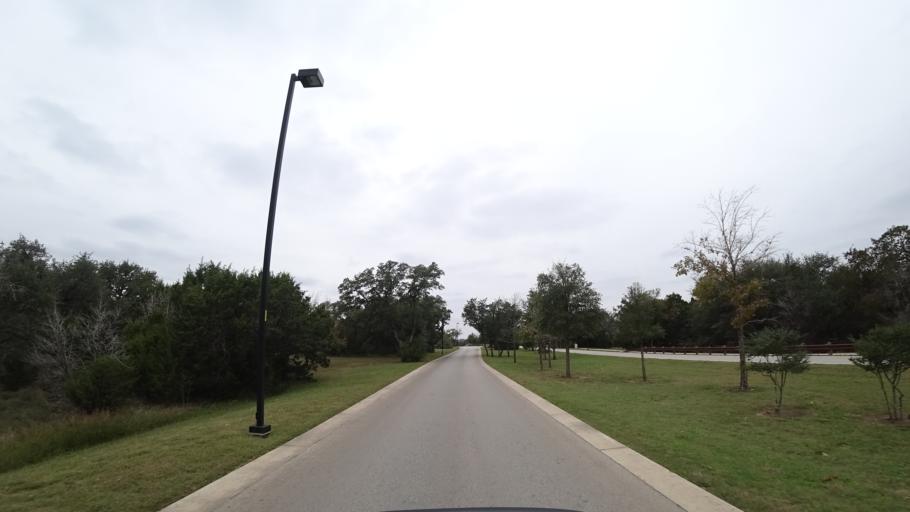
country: US
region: Texas
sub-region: Travis County
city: Shady Hollow
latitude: 30.1790
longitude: -97.9026
